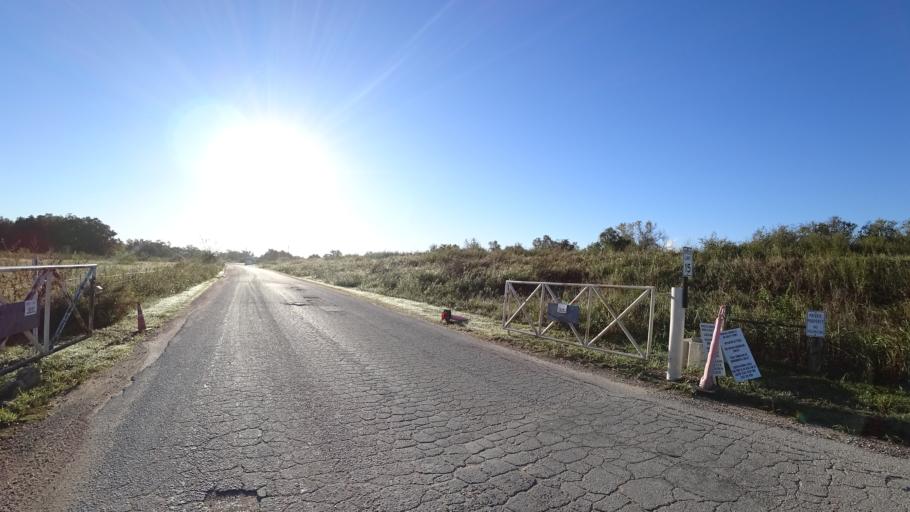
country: US
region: Texas
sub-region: Travis County
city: Hornsby Bend
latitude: 30.2284
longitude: -97.6139
